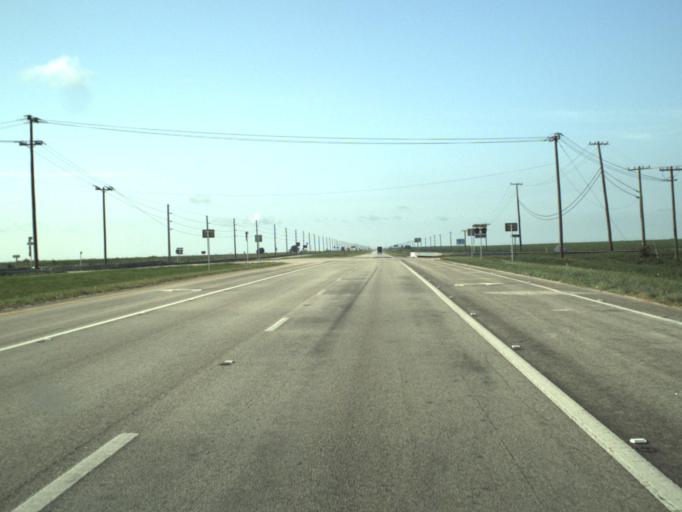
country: US
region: Florida
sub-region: Palm Beach County
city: South Bay
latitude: 26.6111
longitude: -80.7118
